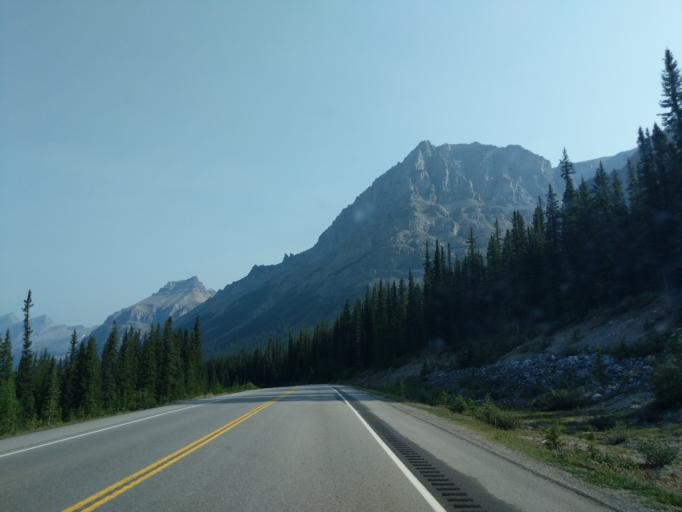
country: CA
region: Alberta
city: Lake Louise
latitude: 51.5944
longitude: -116.3075
